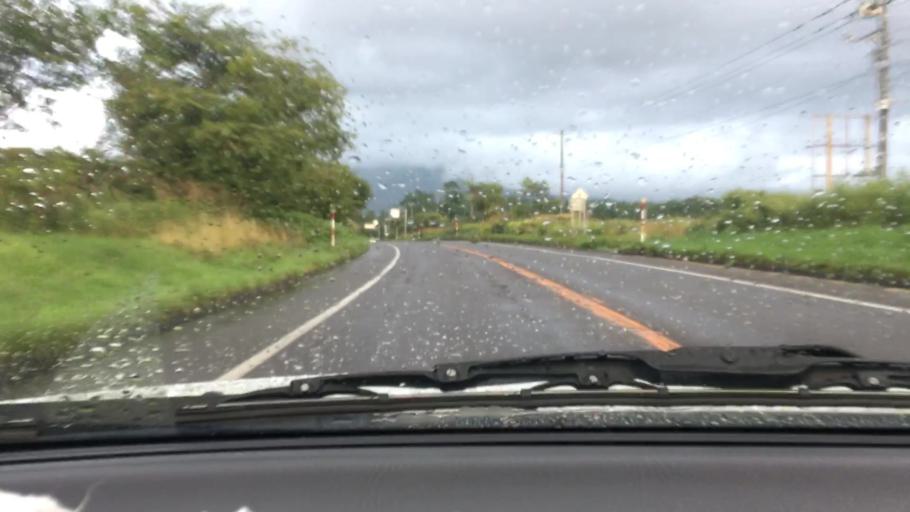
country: JP
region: Hokkaido
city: Nanae
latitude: 42.0811
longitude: 140.5904
